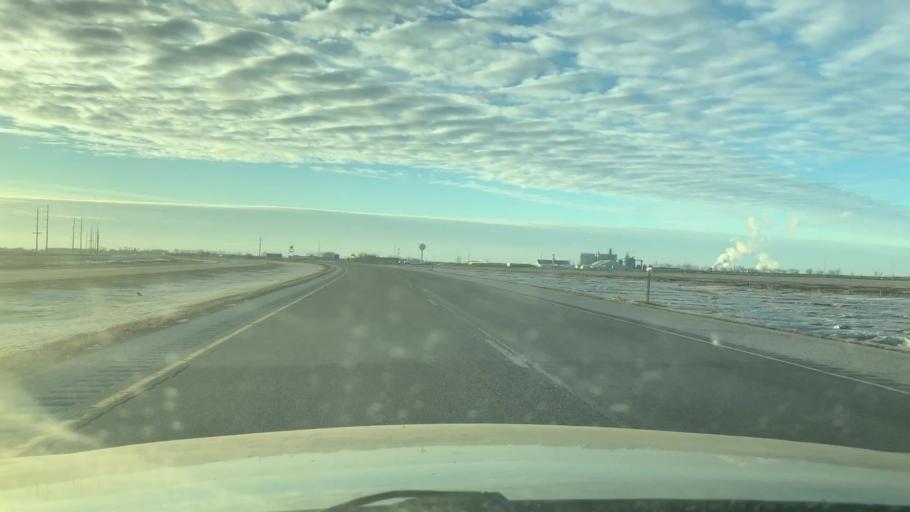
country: US
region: North Dakota
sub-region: Cass County
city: Casselton
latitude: 46.8768
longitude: -97.1898
